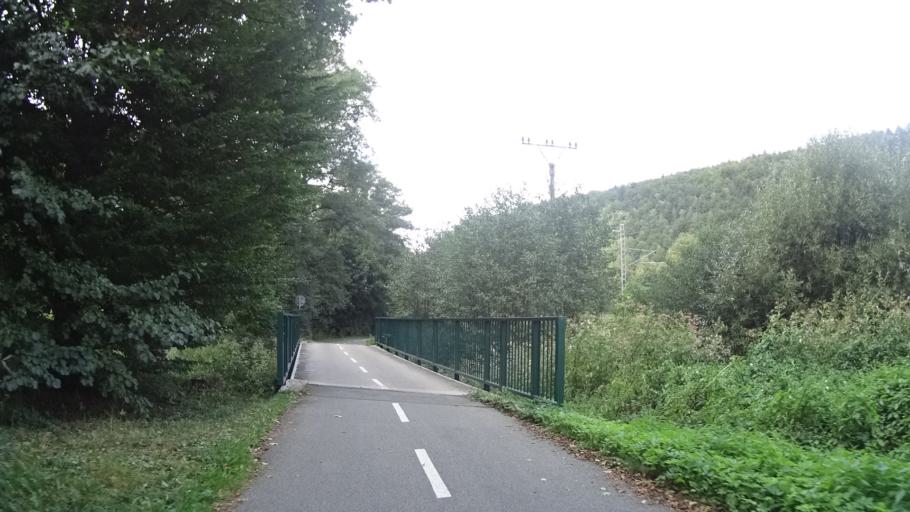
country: CZ
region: Pardubicky
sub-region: Okres Usti nad Orlici
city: Usti nad Orlici
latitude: 49.9865
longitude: 16.4334
